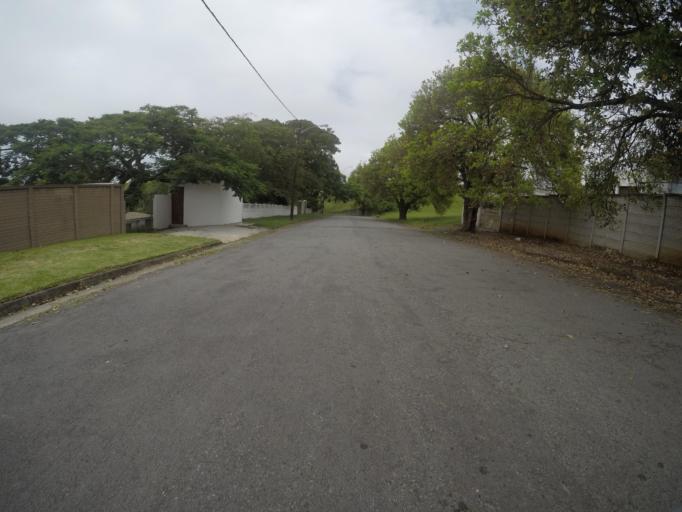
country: ZA
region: Eastern Cape
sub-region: Buffalo City Metropolitan Municipality
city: East London
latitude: -32.9879
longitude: 27.9205
